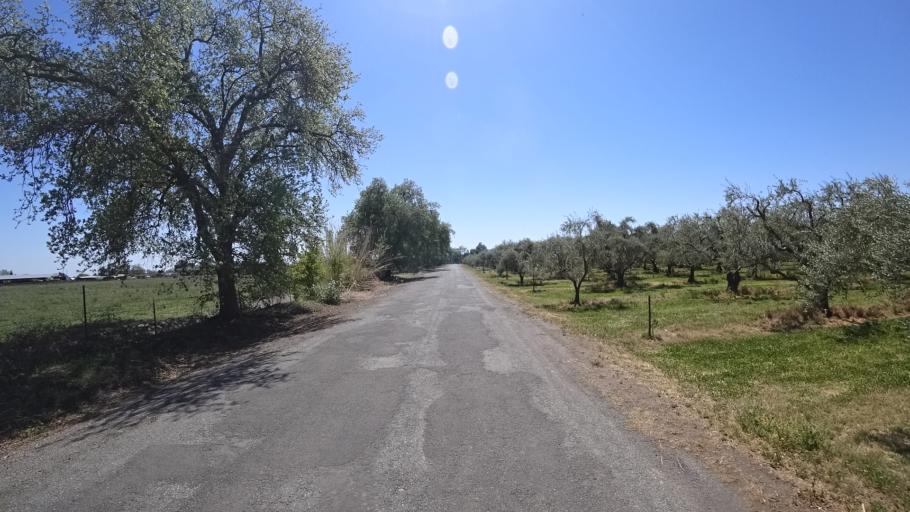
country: US
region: California
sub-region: Glenn County
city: Orland
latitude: 39.7869
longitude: -122.2157
